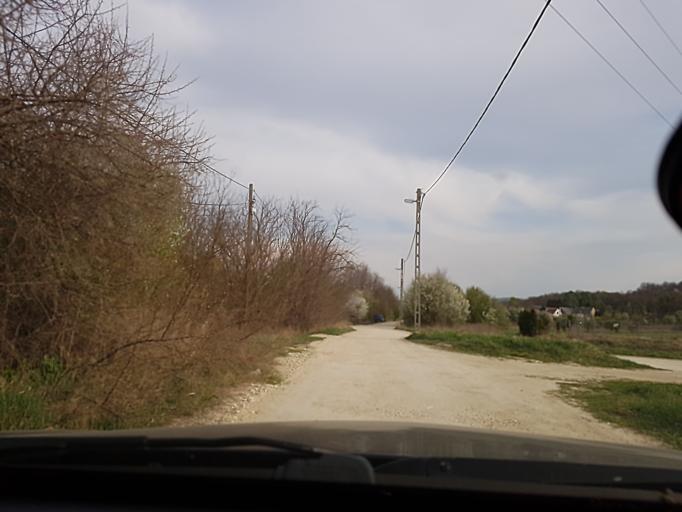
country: HU
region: Pest
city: Piliscsaba
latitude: 47.6332
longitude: 18.8164
